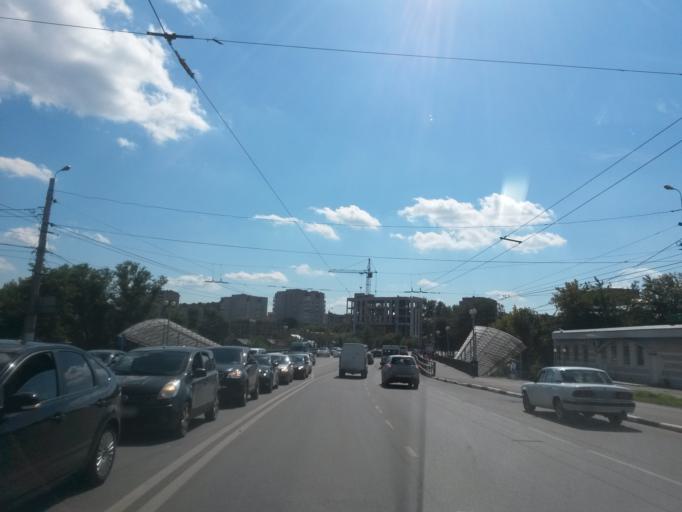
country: RU
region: Ivanovo
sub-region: Gorod Ivanovo
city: Ivanovo
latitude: 57.0057
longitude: 40.9911
